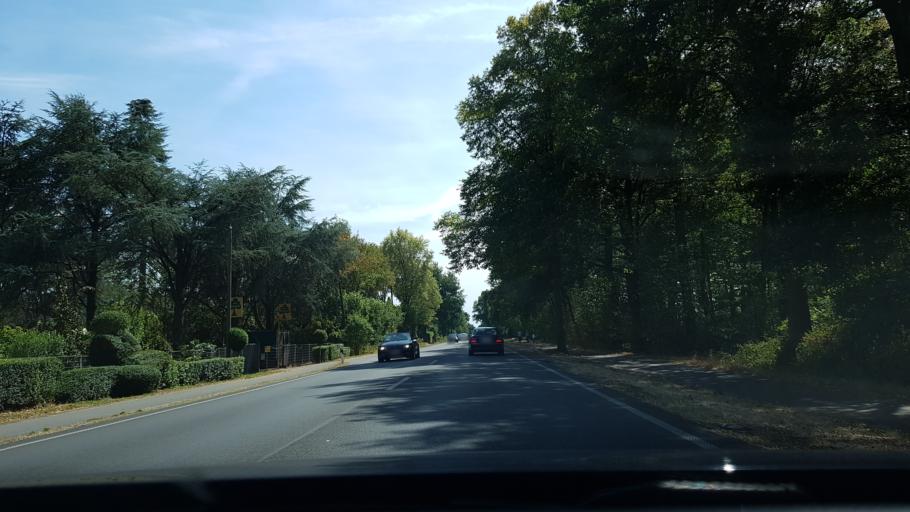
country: DE
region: North Rhine-Westphalia
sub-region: Regierungsbezirk Dusseldorf
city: Voerde
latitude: 51.5885
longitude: 6.7174
